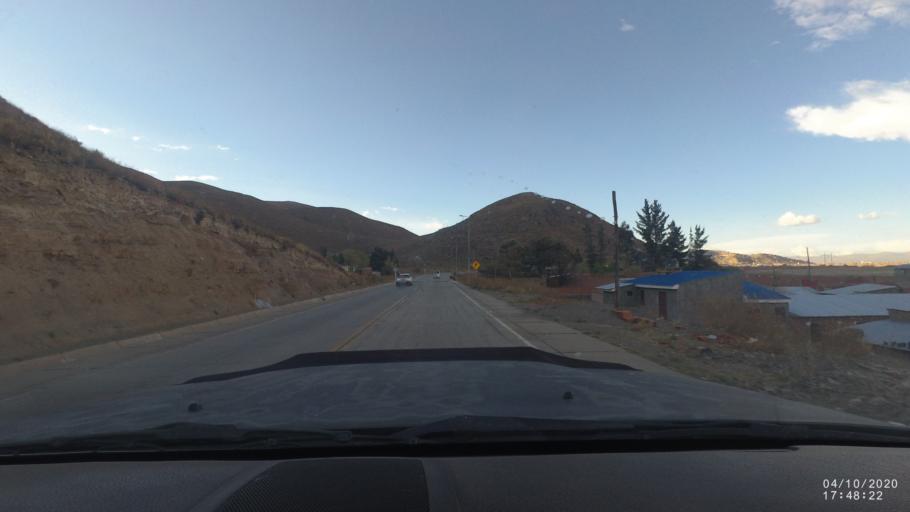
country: BO
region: Oruro
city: Oruro
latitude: -18.0175
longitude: -67.1392
